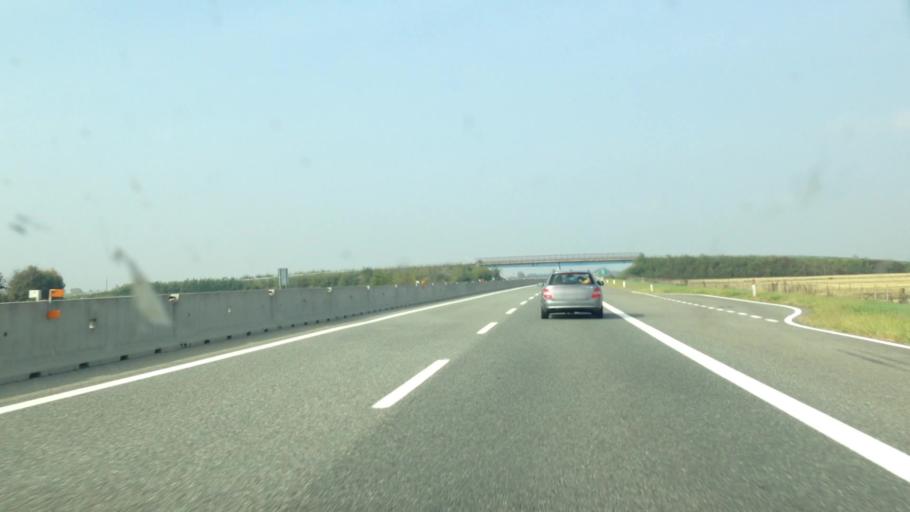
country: IT
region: Piedmont
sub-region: Provincia di Vercelli
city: Sali Vercellese
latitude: 45.3078
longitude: 8.2943
